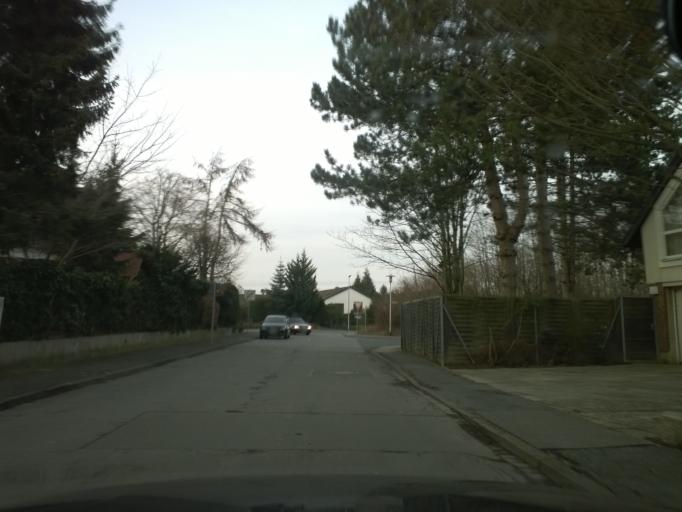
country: DE
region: Lower Saxony
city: Hildesheim
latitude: 52.1301
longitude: 9.9485
